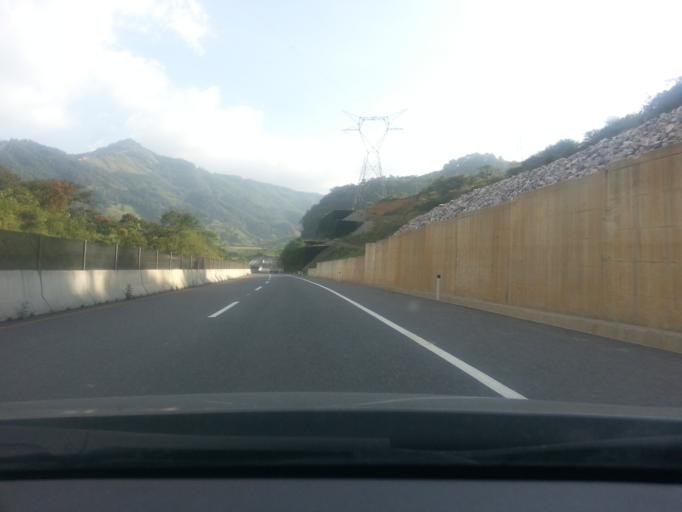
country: MX
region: Puebla
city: Xicotepec de Juarez
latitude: 20.2644
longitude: -98.0082
